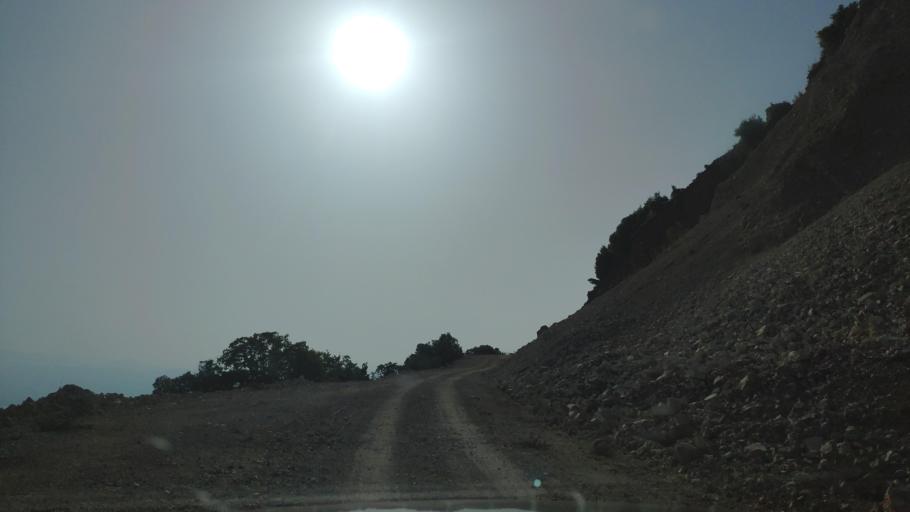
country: GR
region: West Greece
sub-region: Nomos Aitolias kai Akarnanias
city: Monastirakion
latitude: 38.8388
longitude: 20.9751
